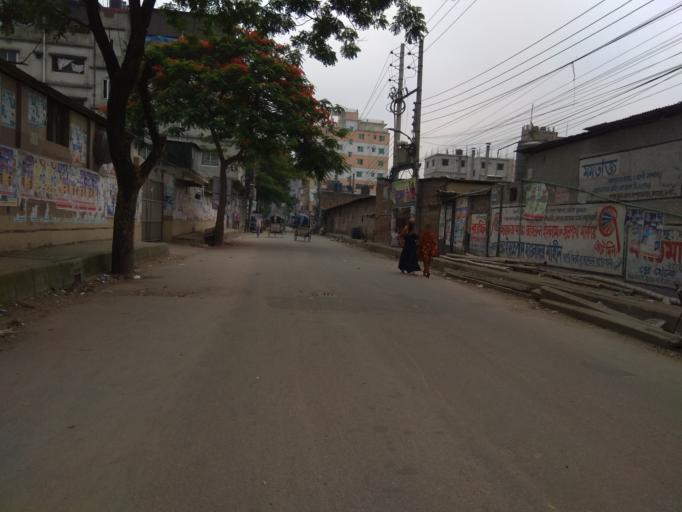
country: BD
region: Dhaka
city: Azimpur
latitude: 23.7115
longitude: 90.3701
